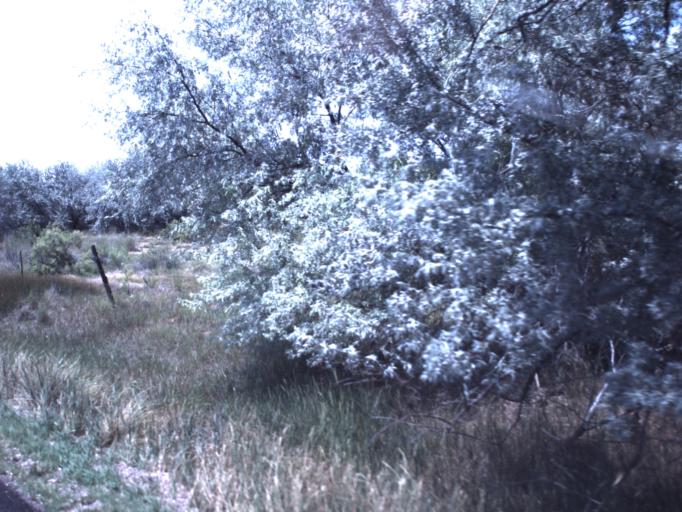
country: US
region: Utah
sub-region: Duchesne County
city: Roosevelt
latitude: 40.4037
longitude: -109.8335
